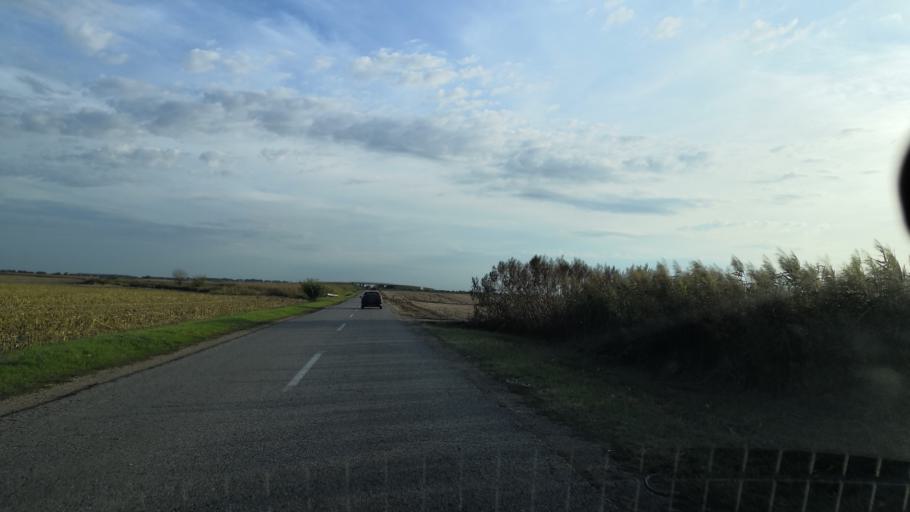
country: RS
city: Novi Karlovci
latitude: 45.0545
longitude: 20.1780
